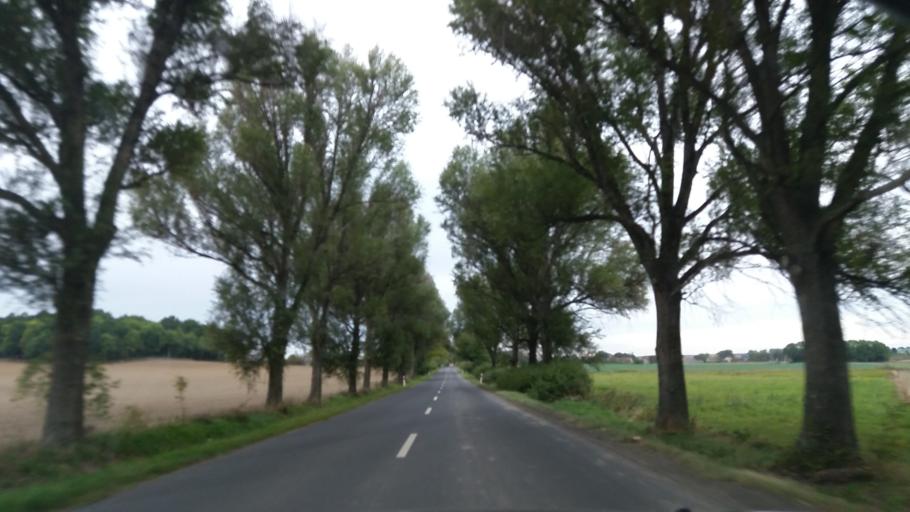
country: PL
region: Lower Silesian Voivodeship
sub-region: Powiat legnicki
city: Legnickie Pole
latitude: 51.1629
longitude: 16.3353
